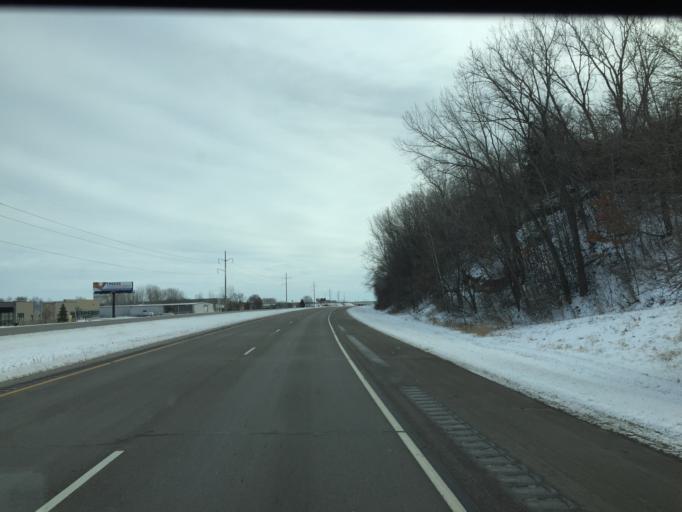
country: US
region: Minnesota
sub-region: Olmsted County
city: Rochester
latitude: 44.0401
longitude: -92.5342
